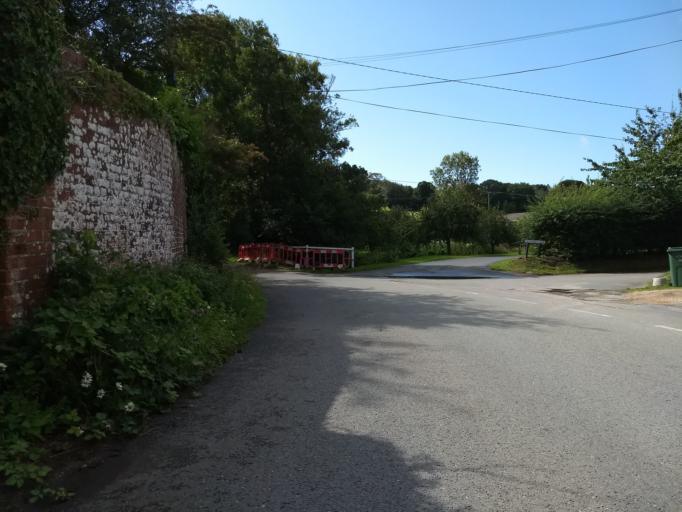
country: GB
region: England
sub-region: Isle of Wight
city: Newport
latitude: 50.6830
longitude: -1.2966
